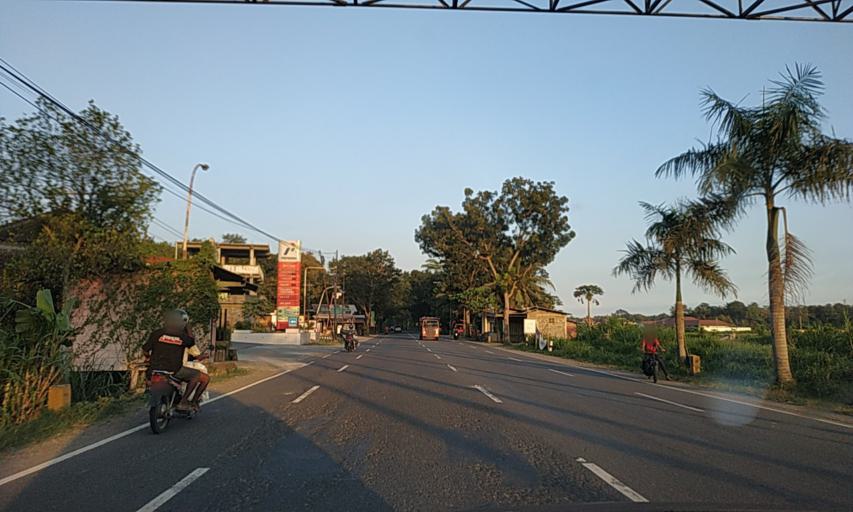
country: ID
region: Daerah Istimewa Yogyakarta
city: Srandakan
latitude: -7.8846
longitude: 110.0496
